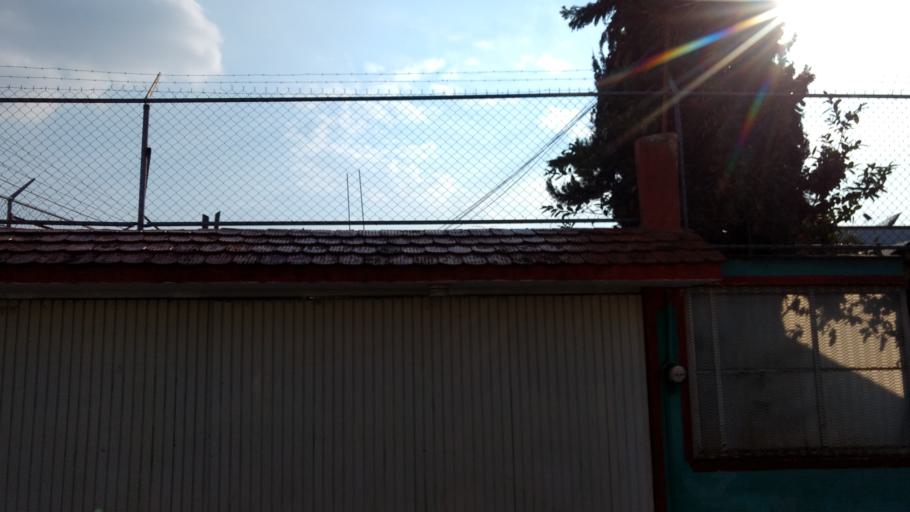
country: MX
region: Guanajuato
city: Leon
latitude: 21.1554
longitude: -101.6715
